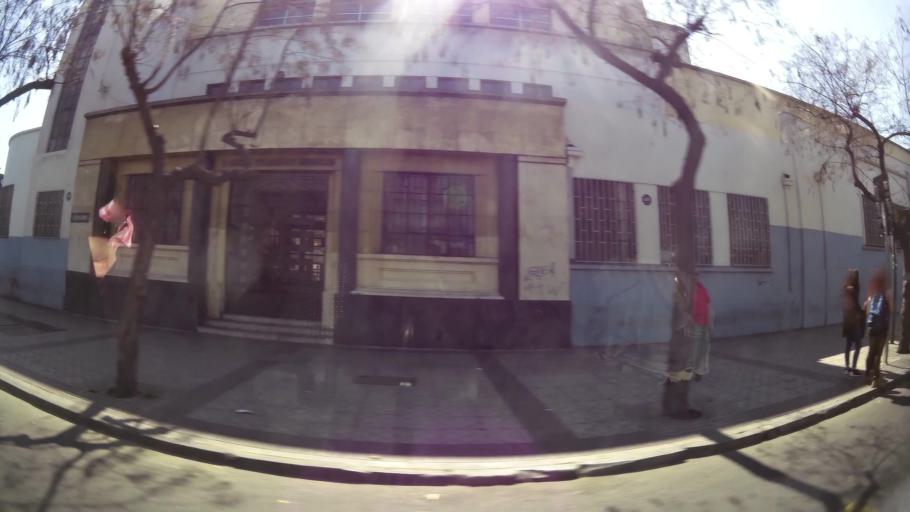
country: CL
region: Santiago Metropolitan
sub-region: Provincia de Santiago
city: Santiago
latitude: -33.4593
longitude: -70.6489
